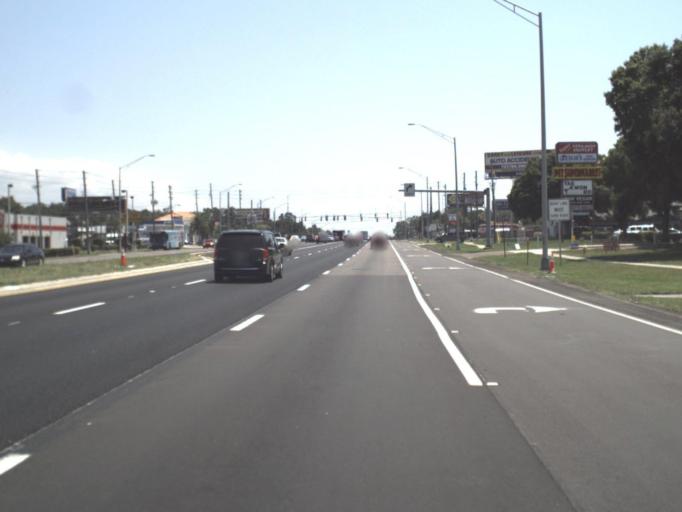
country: US
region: Florida
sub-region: Pinellas County
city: Saint George
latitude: 28.0697
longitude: -82.7390
